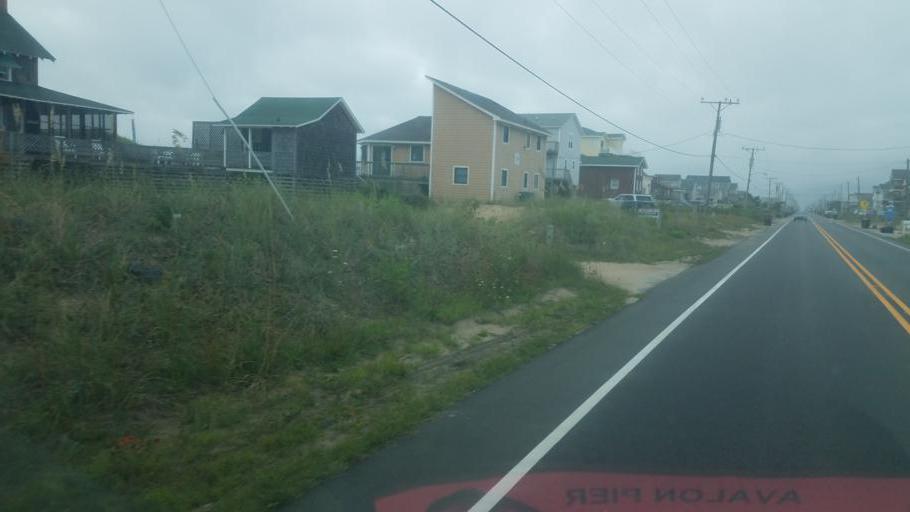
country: US
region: North Carolina
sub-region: Dare County
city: Kill Devil Hills
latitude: 36.0405
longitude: -75.6732
